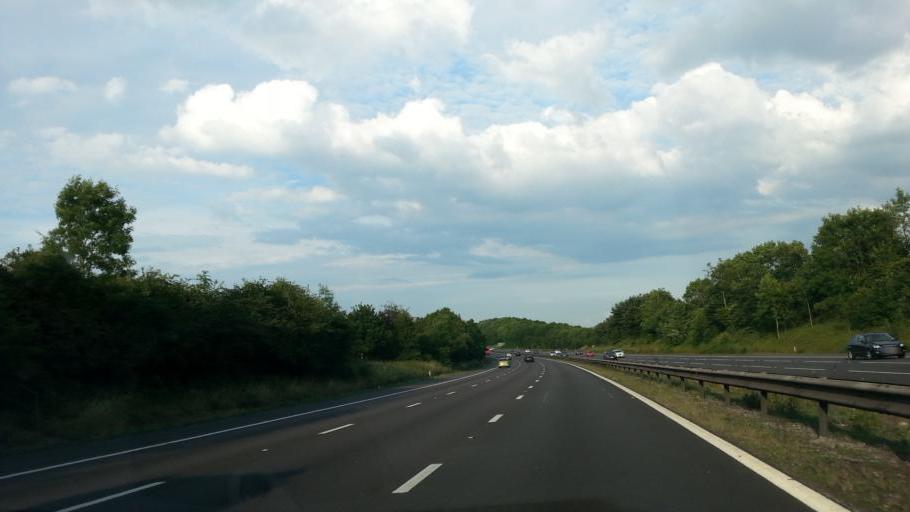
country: GB
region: England
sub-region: Worcestershire
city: Barnt Green
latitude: 52.3531
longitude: -2.0048
